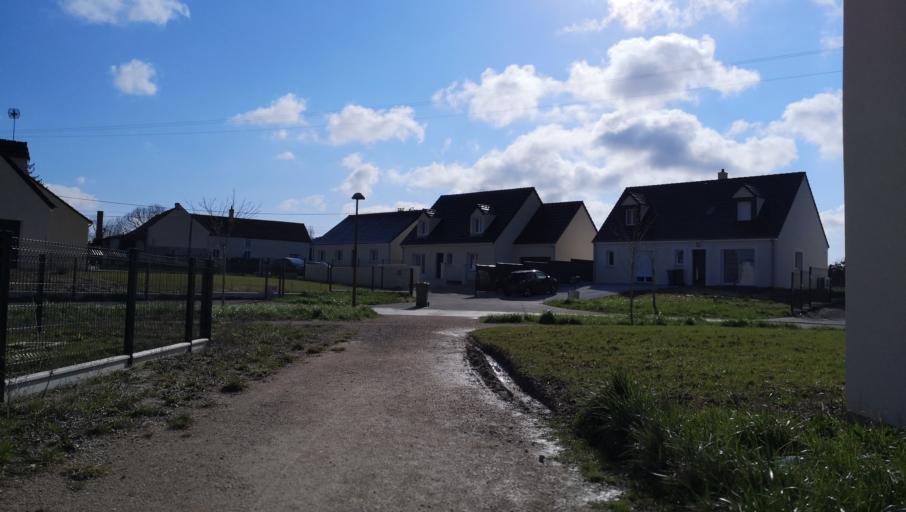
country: FR
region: Centre
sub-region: Departement du Loiret
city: Chanteau
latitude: 47.9644
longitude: 1.9736
